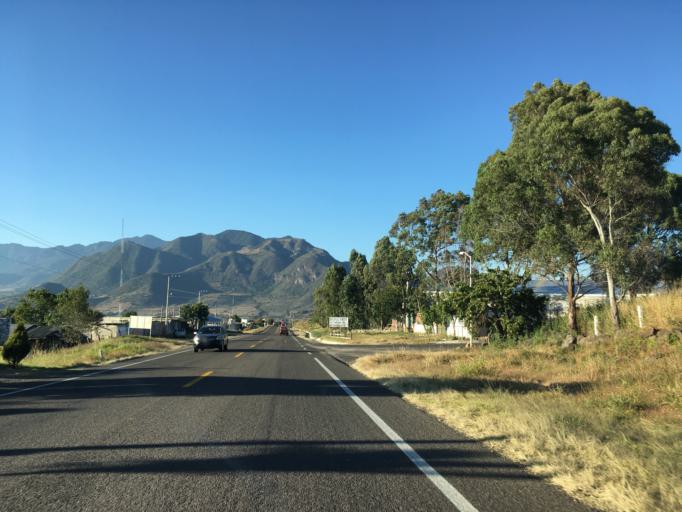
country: MX
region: Michoacan
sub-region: Tuxpan
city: La Soledad
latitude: 19.5293
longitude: -100.4742
